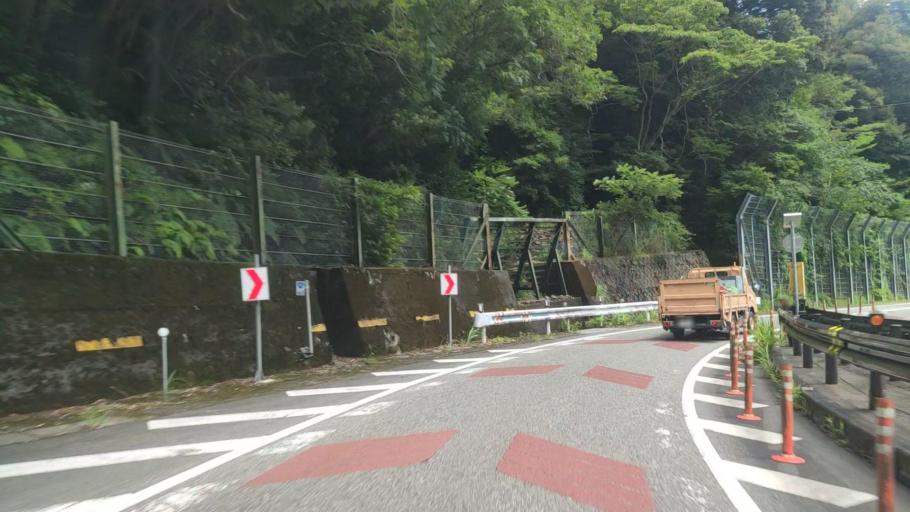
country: JP
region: Mie
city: Owase
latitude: 33.9219
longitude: 136.1010
